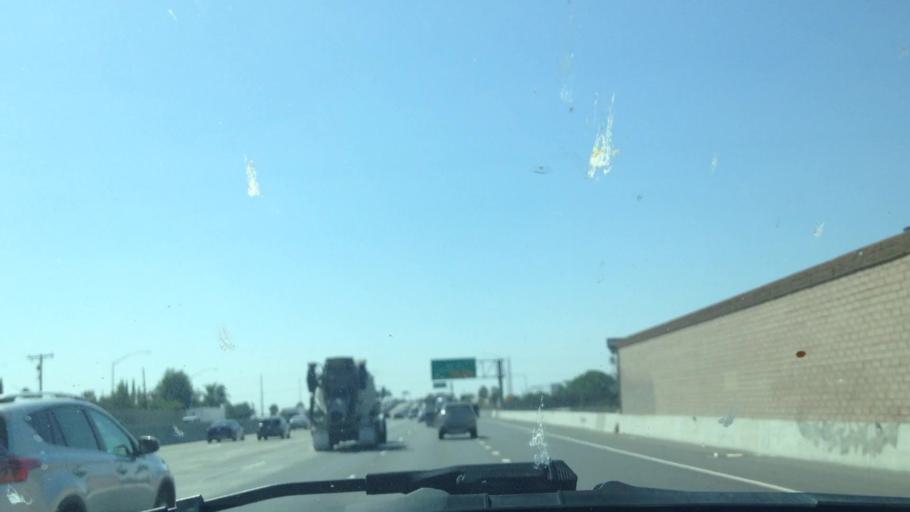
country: US
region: California
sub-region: Orange County
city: Anaheim
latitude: 33.8535
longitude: -117.9021
